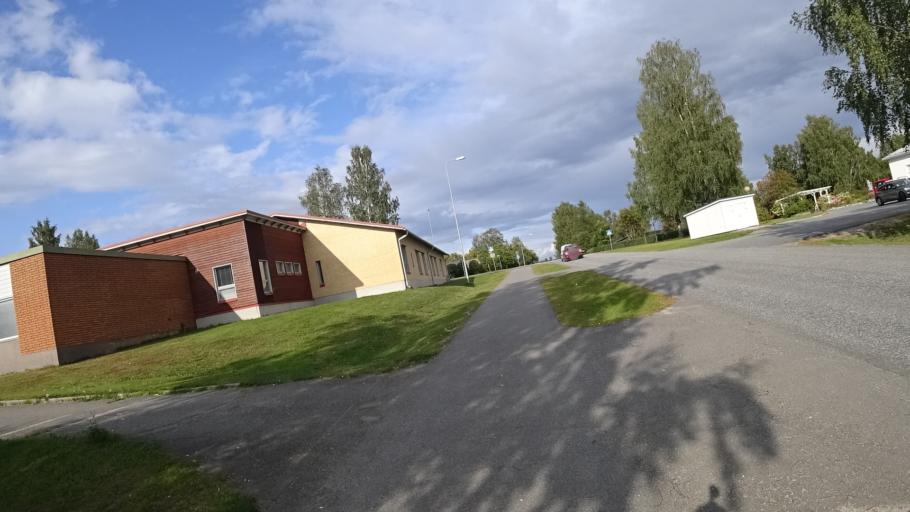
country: FI
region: North Karelia
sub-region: Joensuu
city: Ilomantsi
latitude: 62.6691
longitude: 30.9219
